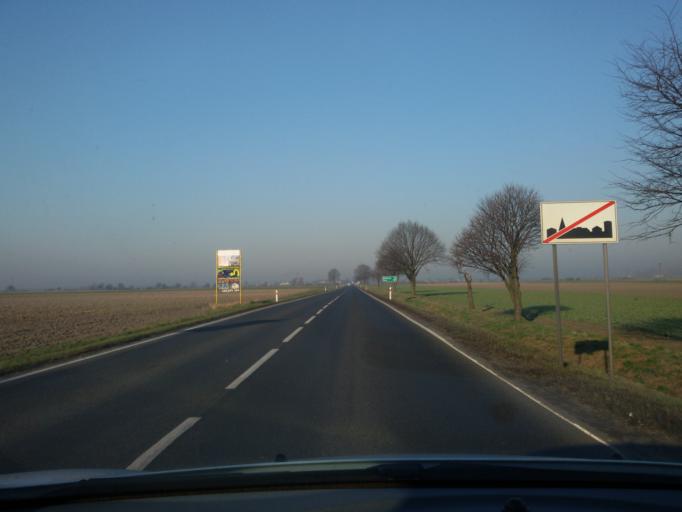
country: PL
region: Greater Poland Voivodeship
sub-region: Powiat leszczynski
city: Swieciechowa
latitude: 51.8250
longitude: 16.4816
